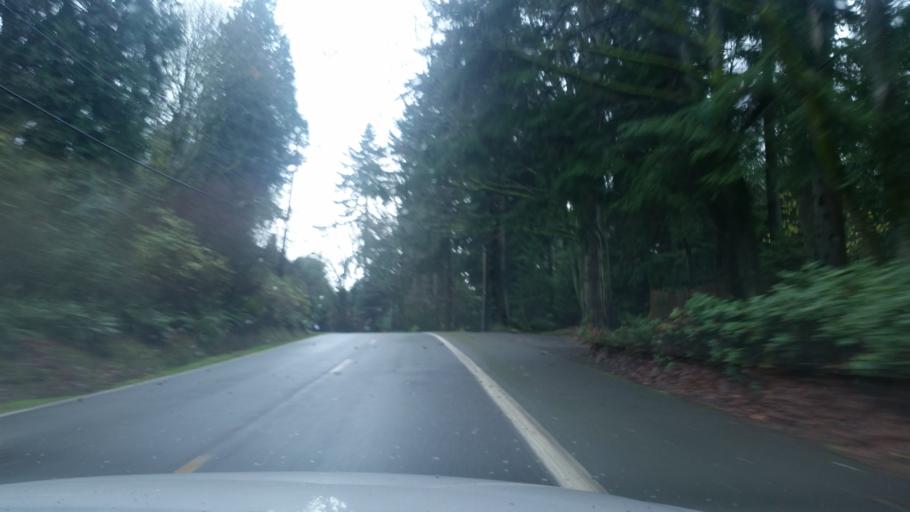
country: US
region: Washington
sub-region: Snohomish County
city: Woodway
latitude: 47.7965
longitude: -122.3825
